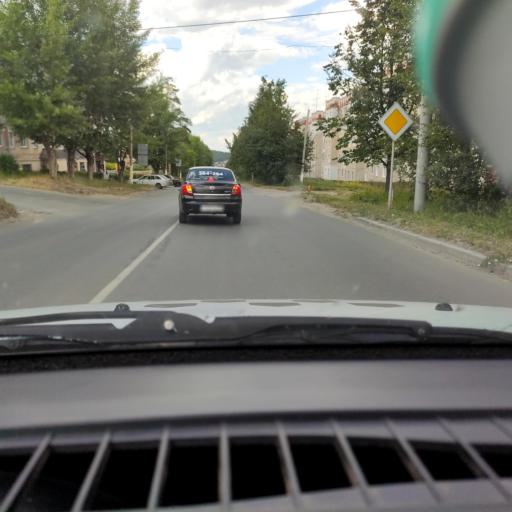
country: RU
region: Chelyabinsk
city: Miass
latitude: 55.0793
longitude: 60.0939
